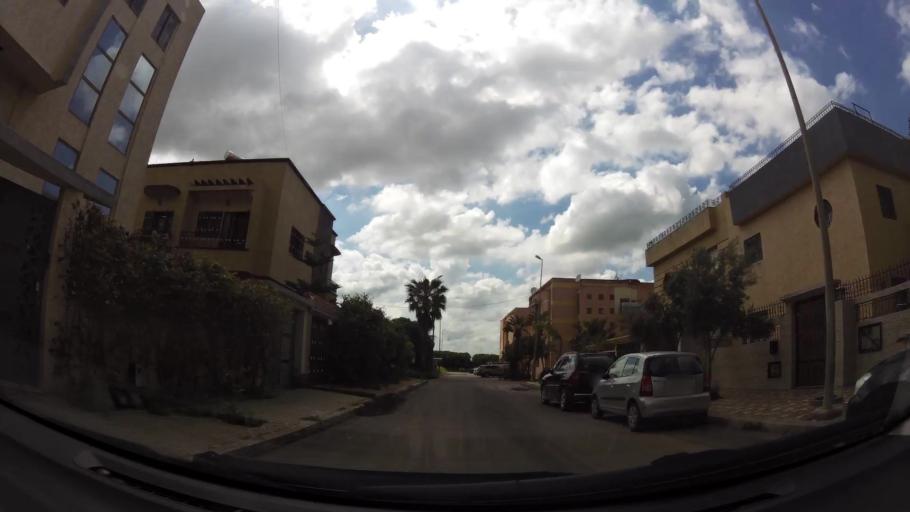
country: MA
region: Chaouia-Ouardigha
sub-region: Settat Province
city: Berrechid
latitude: 33.2794
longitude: -7.5933
